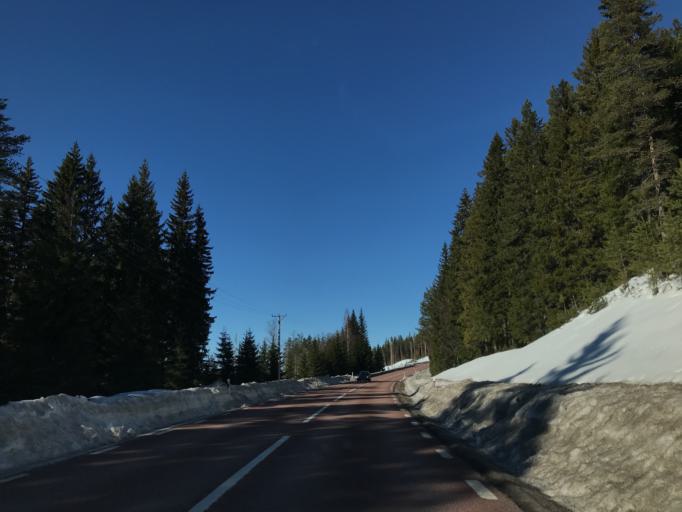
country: SE
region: Vaermland
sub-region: Filipstads Kommun
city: Lesjofors
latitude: 60.2257
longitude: 14.1817
